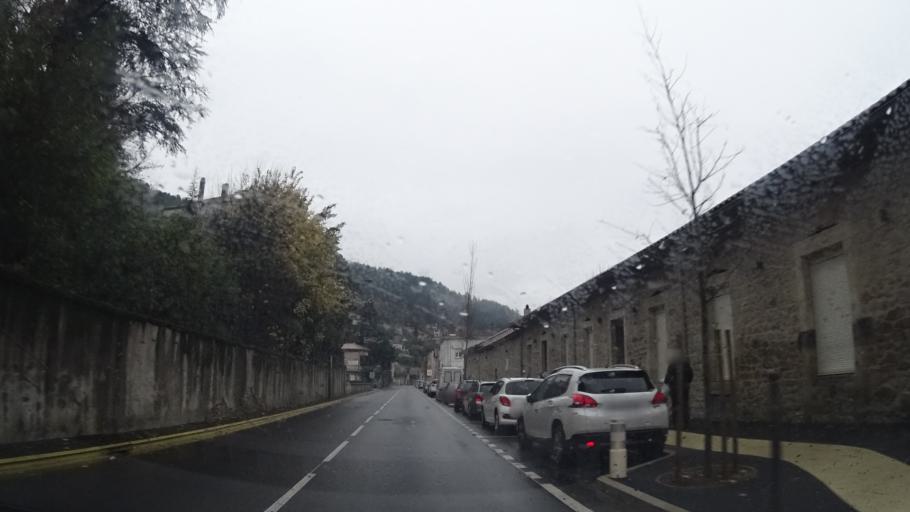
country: FR
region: Rhone-Alpes
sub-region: Departement de l'Ardeche
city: Vals-les-Bains
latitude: 44.6650
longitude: 4.3665
